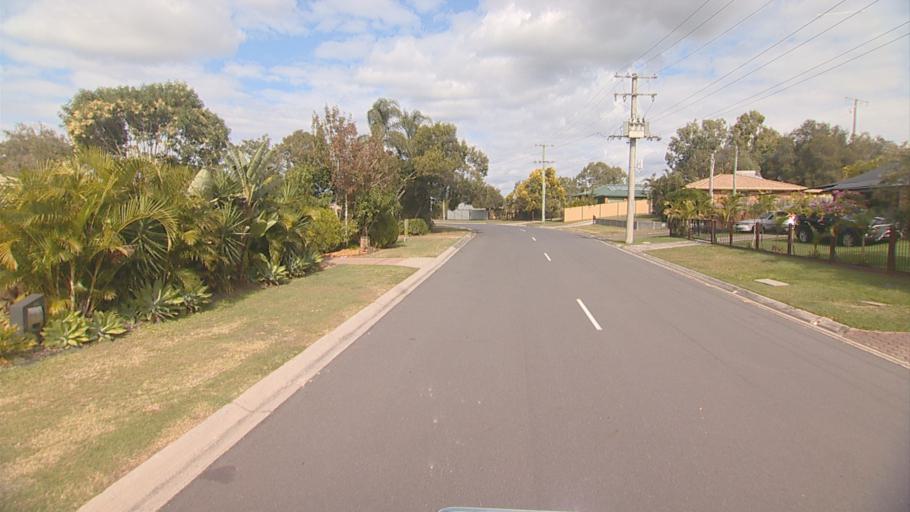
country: AU
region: Queensland
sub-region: Logan
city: Windaroo
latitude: -27.7369
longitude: 153.2086
